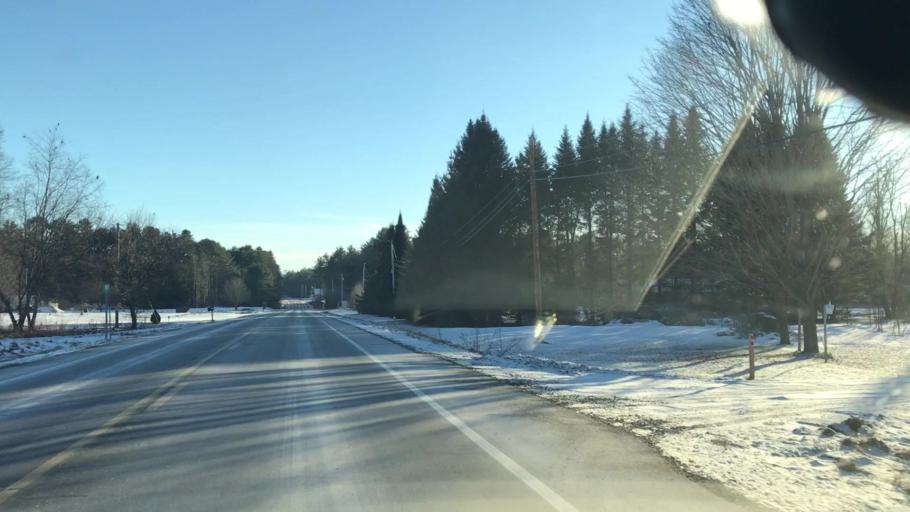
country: US
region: New Hampshire
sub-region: Grafton County
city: Orford
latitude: 43.8784
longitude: -72.1559
